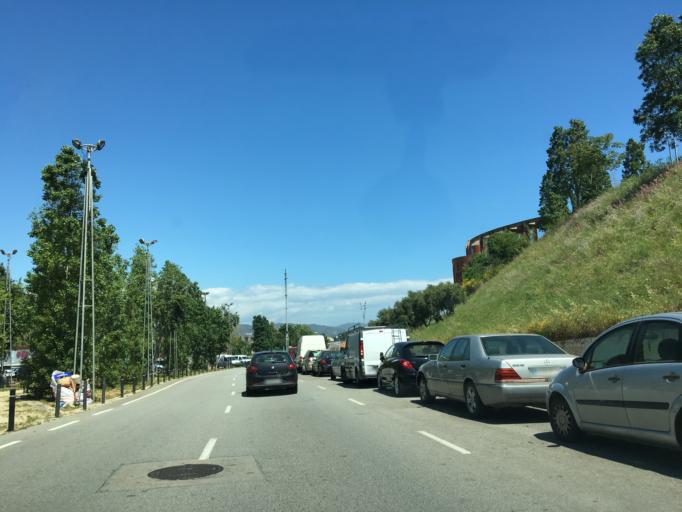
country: ES
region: Catalonia
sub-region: Provincia de Barcelona
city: Horta-Guinardo
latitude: 41.4249
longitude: 2.1485
